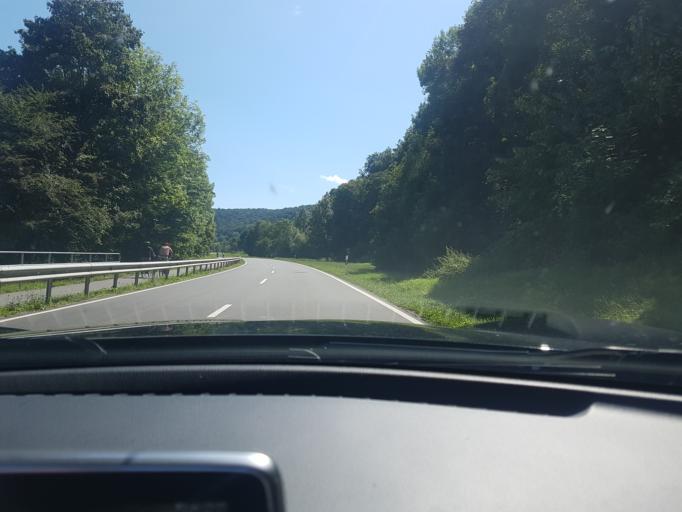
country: DE
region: Baden-Wuerttemberg
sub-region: Karlsruhe Region
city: Hassmersheim
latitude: 49.2903
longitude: 9.1299
